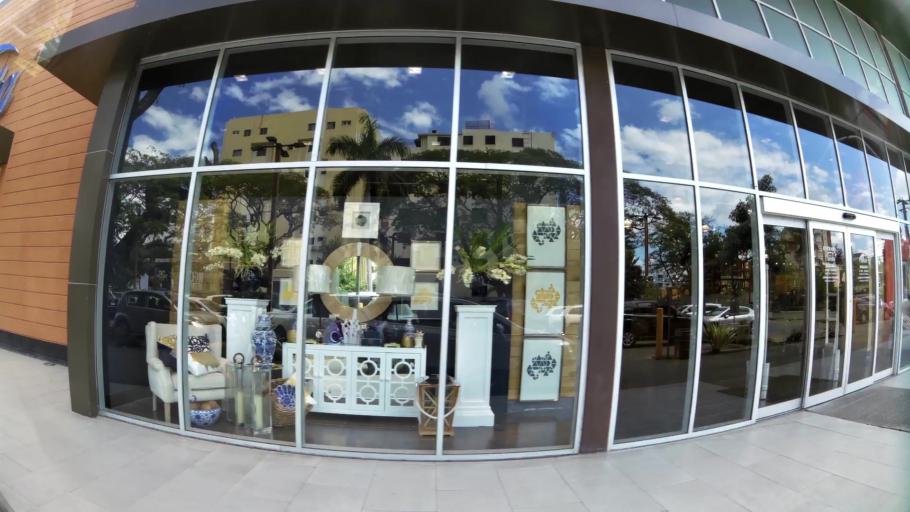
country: DO
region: Santiago
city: Santiago de los Caballeros
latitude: 19.4571
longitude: -70.6760
